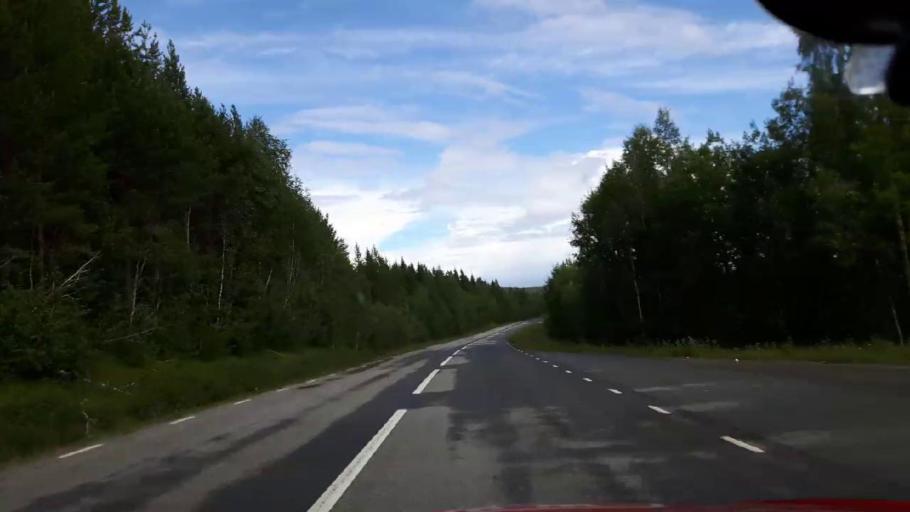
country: SE
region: Jaemtland
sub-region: Stroemsunds Kommun
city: Stroemsund
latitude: 64.3390
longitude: 15.0242
